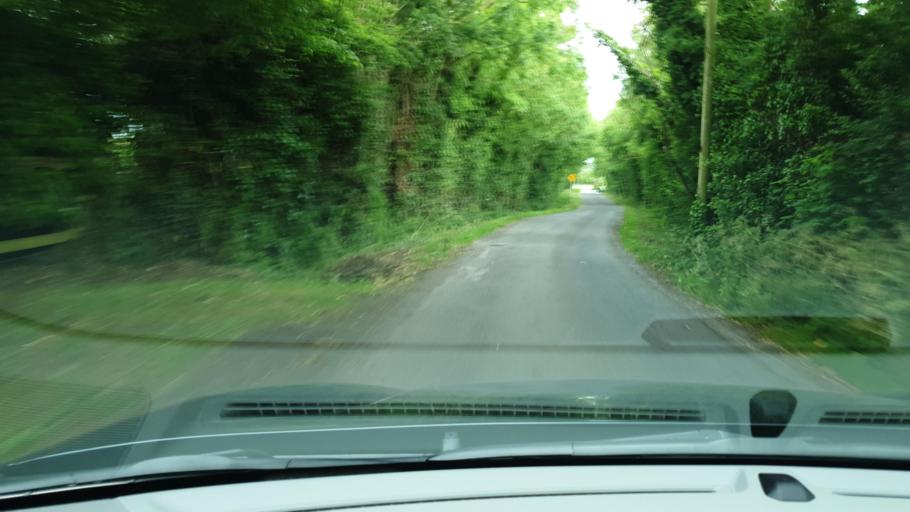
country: IE
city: Confey
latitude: 53.4002
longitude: -6.5073
